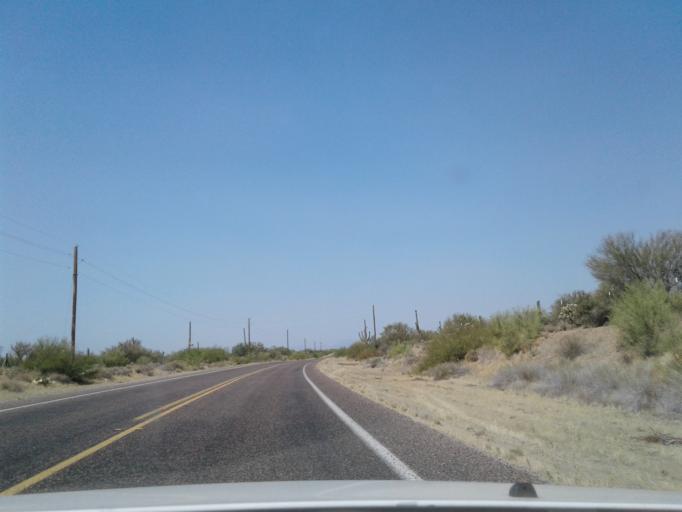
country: US
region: Arizona
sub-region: Pima County
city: Catalina
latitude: 32.6464
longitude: -111.1102
